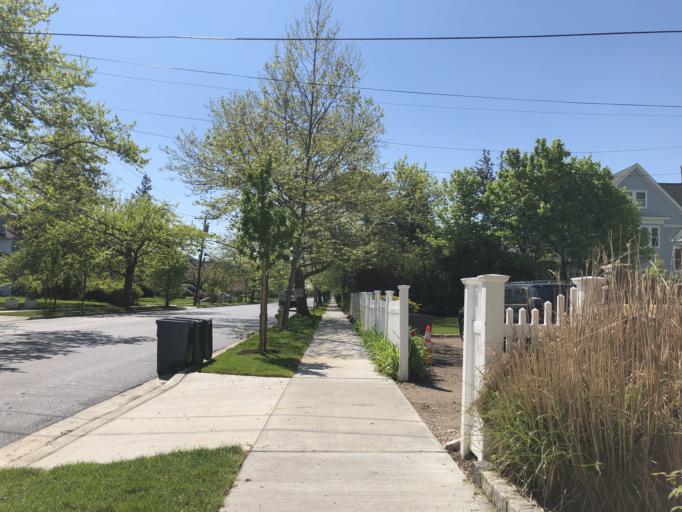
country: US
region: New York
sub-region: Suffolk County
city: Bay Shore
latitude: 40.7202
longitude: -73.2465
